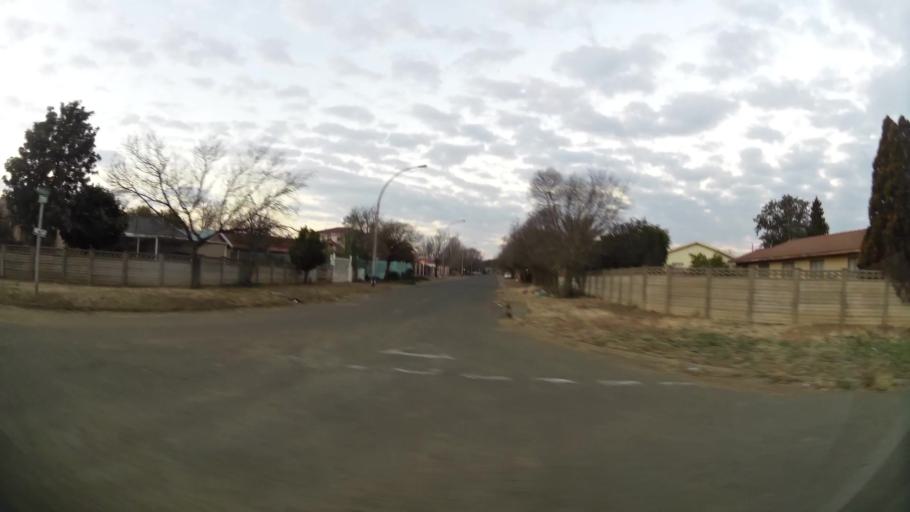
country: ZA
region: Orange Free State
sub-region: Mangaung Metropolitan Municipality
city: Bloemfontein
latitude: -29.1755
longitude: 26.1882
